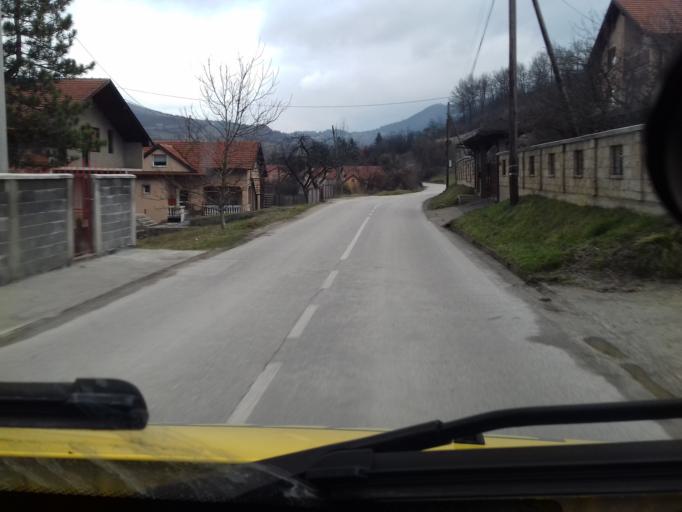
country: BA
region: Federation of Bosnia and Herzegovina
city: Zenica
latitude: 44.1797
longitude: 17.9658
